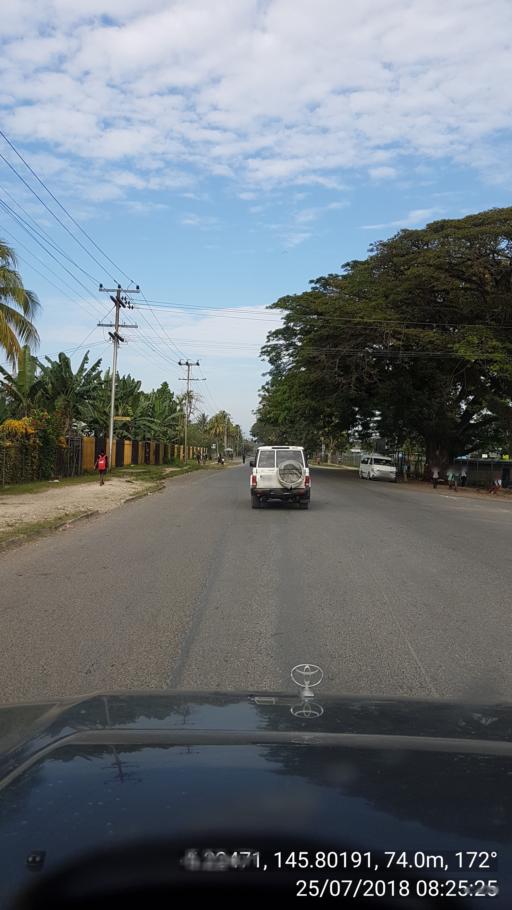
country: PG
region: Madang
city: Madang
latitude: -5.2247
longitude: 145.8019
